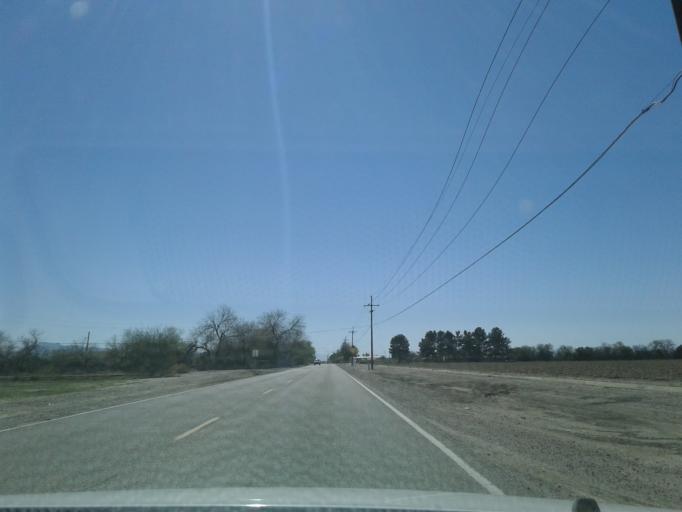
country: US
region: Arizona
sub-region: Pima County
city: Marana
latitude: 32.4420
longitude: -111.2341
